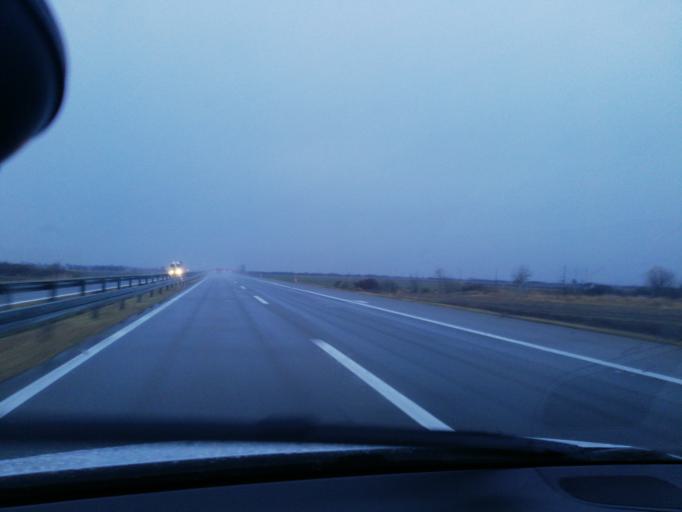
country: RS
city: Macvanska Mitrovica
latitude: 45.0140
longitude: 19.5755
